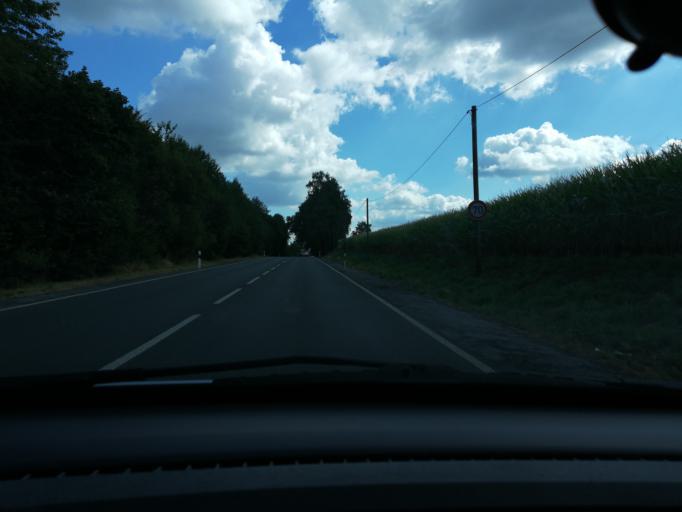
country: DE
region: North Rhine-Westphalia
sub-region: Regierungsbezirk Arnsberg
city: Schwelm
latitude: 51.3119
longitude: 7.3025
